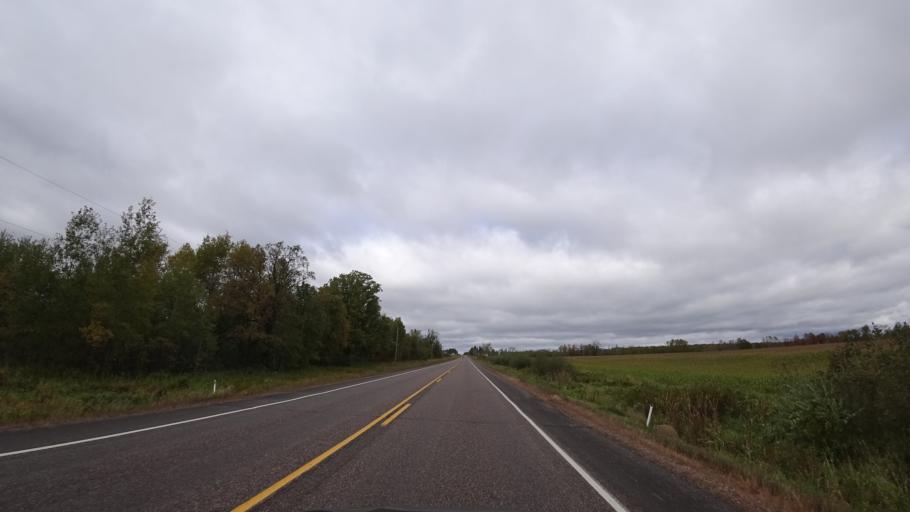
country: US
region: Wisconsin
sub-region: Rusk County
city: Ladysmith
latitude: 45.3968
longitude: -91.1102
